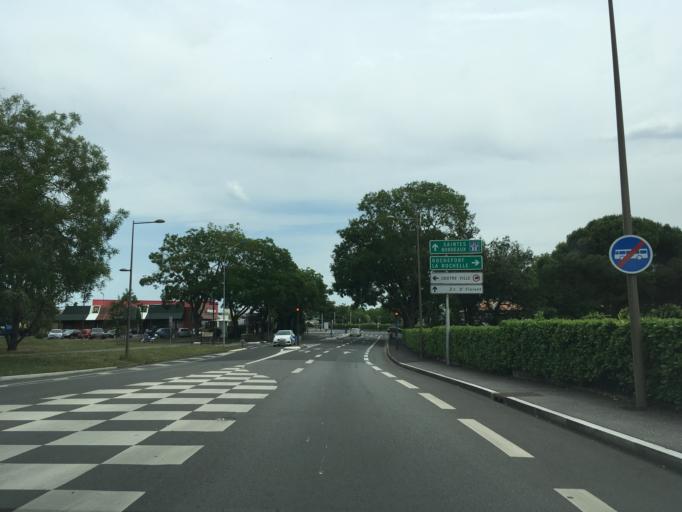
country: FR
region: Poitou-Charentes
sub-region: Departement des Deux-Sevres
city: Niort
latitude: 46.3129
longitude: -0.4802
